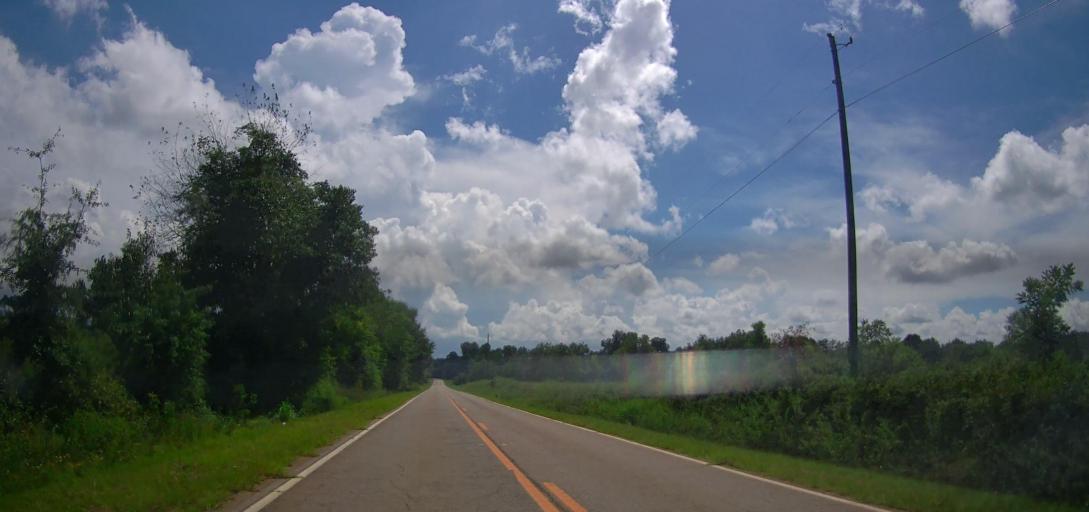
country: US
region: Georgia
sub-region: Peach County
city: Fort Valley
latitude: 32.5302
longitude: -83.8028
